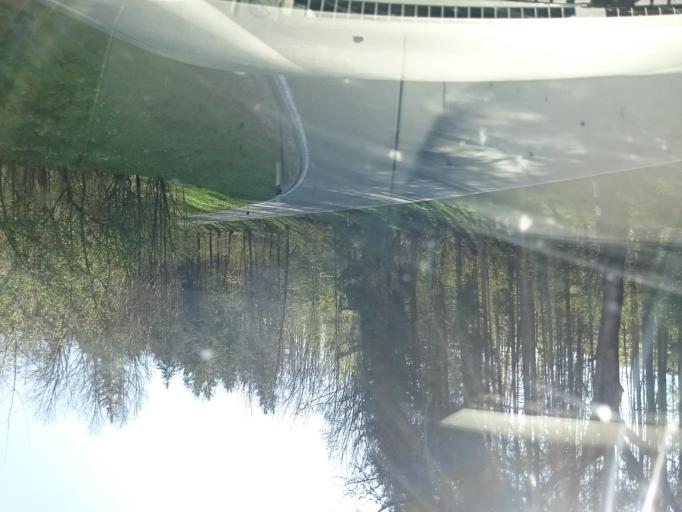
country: DE
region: Bavaria
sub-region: Upper Bavaria
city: Ohlstadt
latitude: 47.6604
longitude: 11.2466
